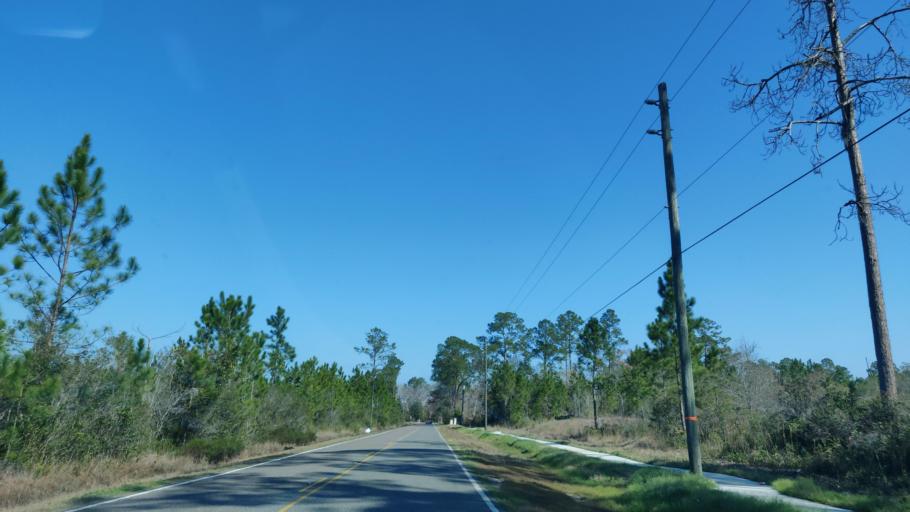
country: US
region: Florida
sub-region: Duval County
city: Baldwin
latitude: 30.2053
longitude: -81.9662
